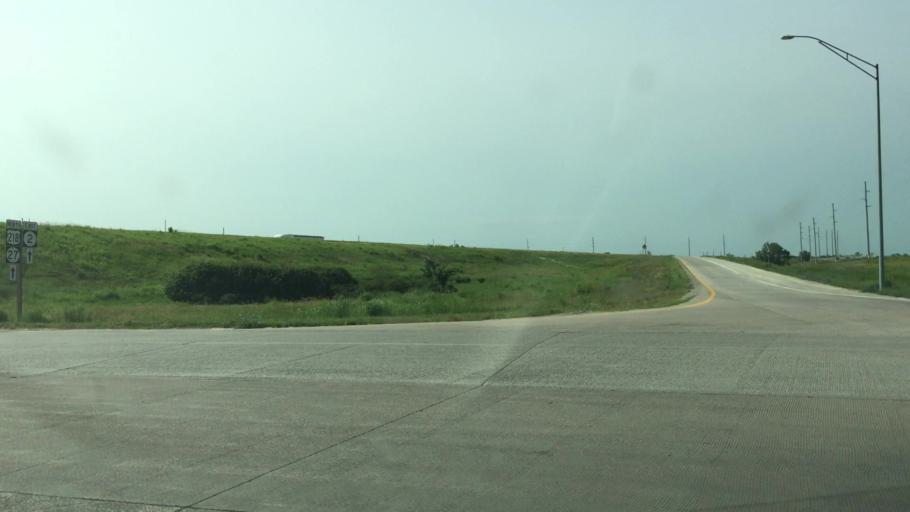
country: US
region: Illinois
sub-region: Hancock County
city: Nauvoo
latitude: 40.6392
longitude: -91.5571
